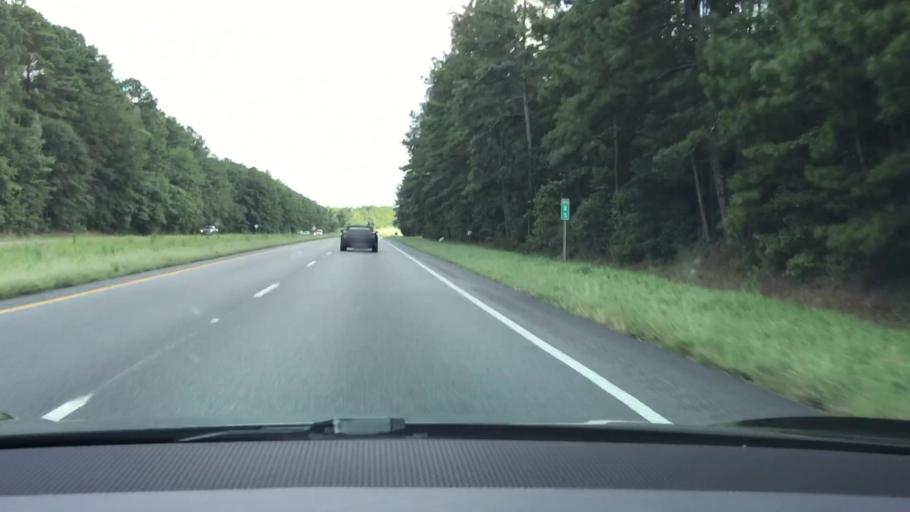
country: US
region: Alabama
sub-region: Pike County
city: Troy
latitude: 31.9157
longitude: -86.0143
